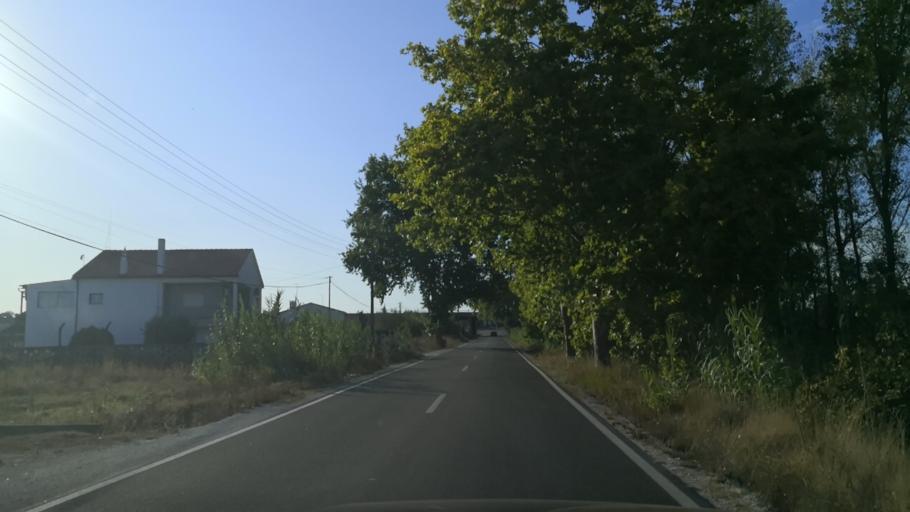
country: PT
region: Santarem
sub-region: Santarem
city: Santarem
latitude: 39.3121
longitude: -8.6685
